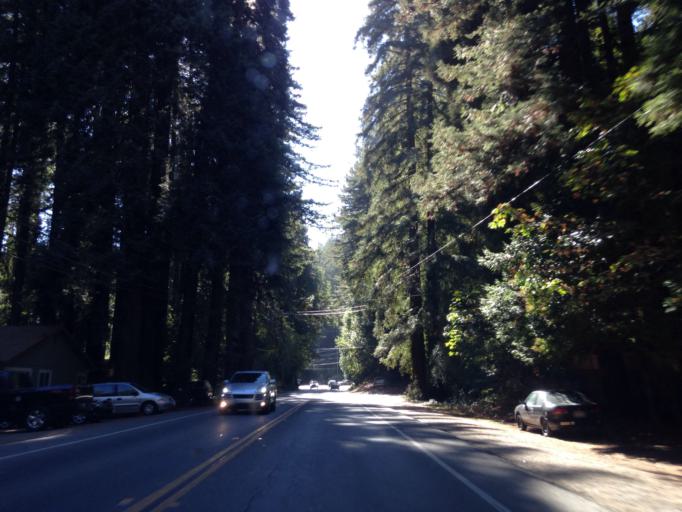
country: US
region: California
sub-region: Sonoma County
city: Guerneville
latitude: 38.4936
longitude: -123.0123
